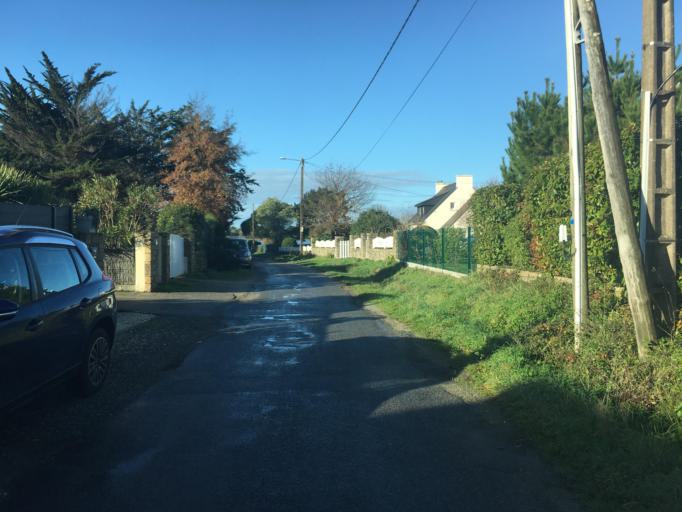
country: FR
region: Brittany
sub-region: Departement du Morbihan
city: Sene
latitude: 47.5740
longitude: -2.7149
